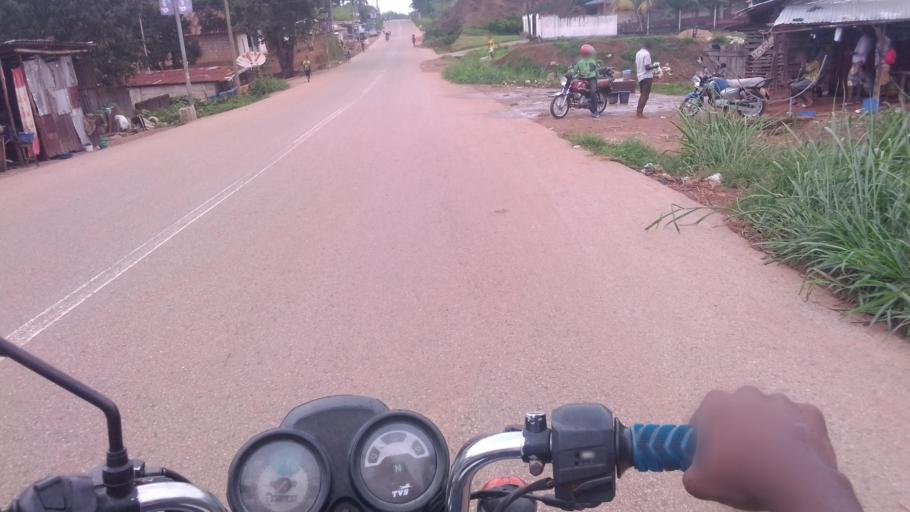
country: SL
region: Eastern Province
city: Kenema
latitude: 7.8754
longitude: -11.1799
